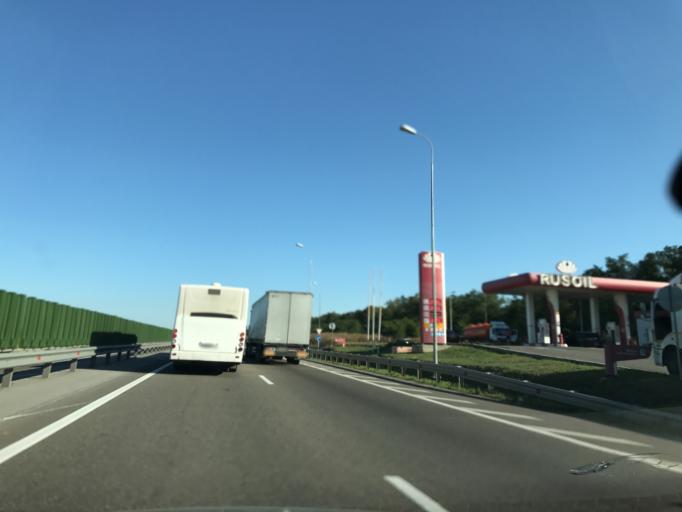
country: RU
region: Rostov
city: Tarasovskiy
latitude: 48.6448
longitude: 40.3576
